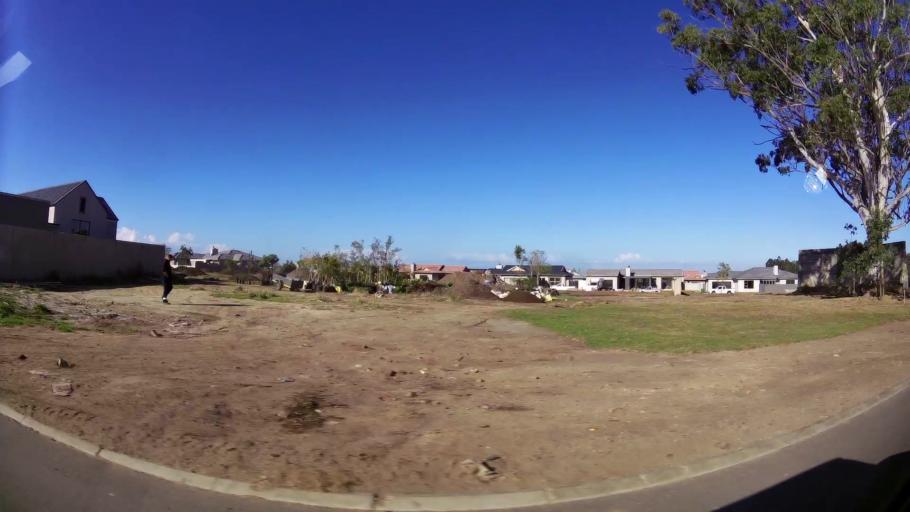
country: ZA
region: Western Cape
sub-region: Eden District Municipality
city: George
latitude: -33.9598
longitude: 22.4203
